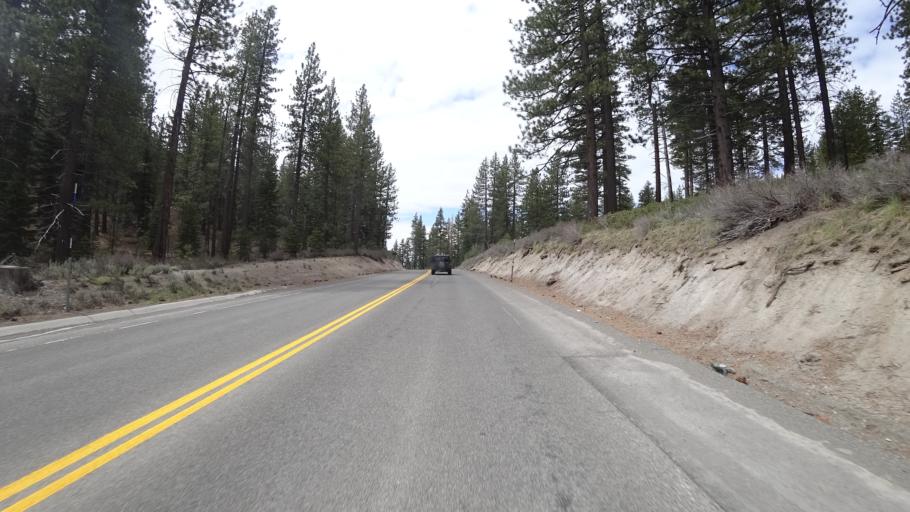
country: US
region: Nevada
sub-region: Washoe County
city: Incline Village
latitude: 39.1342
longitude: -119.9305
